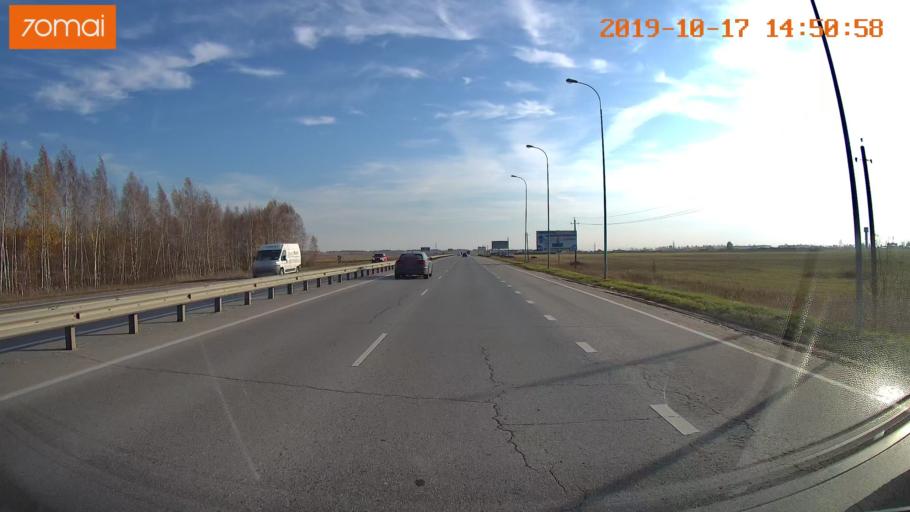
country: RU
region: Rjazan
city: Polyany
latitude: 54.7263
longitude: 39.8457
